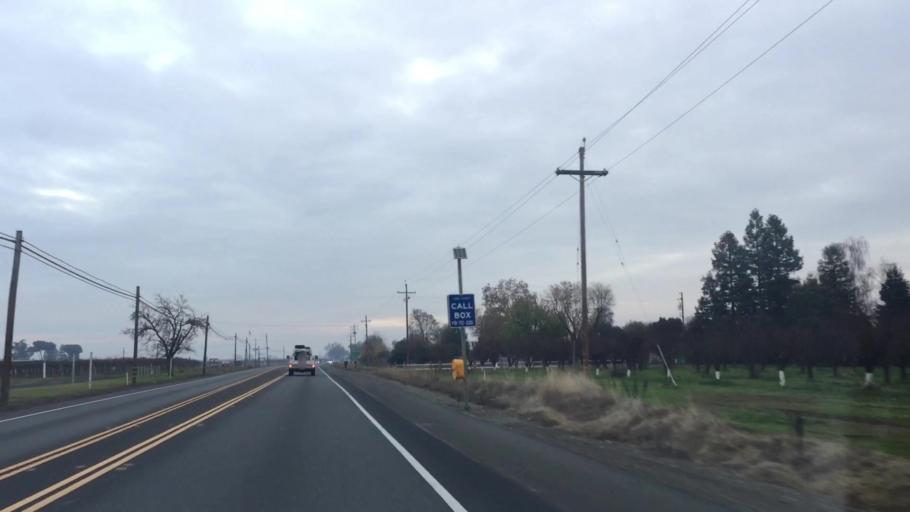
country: US
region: California
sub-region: Sutter County
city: Live Oak
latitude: 39.2536
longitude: -121.5989
